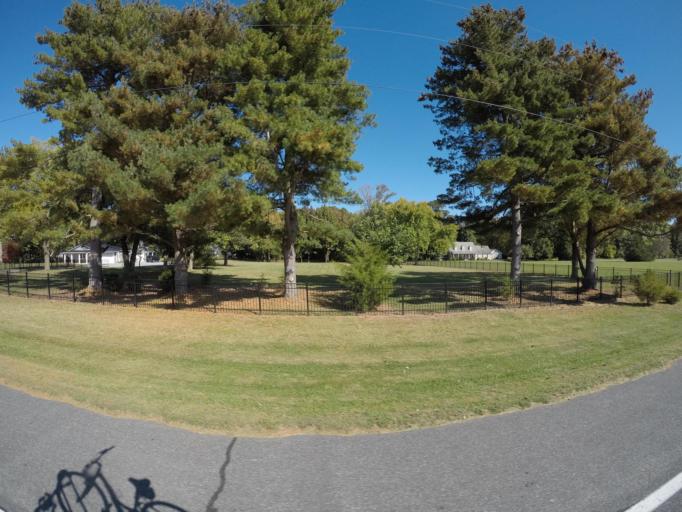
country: US
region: Delaware
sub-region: Sussex County
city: Bridgeville
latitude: 38.8017
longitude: -75.5628
